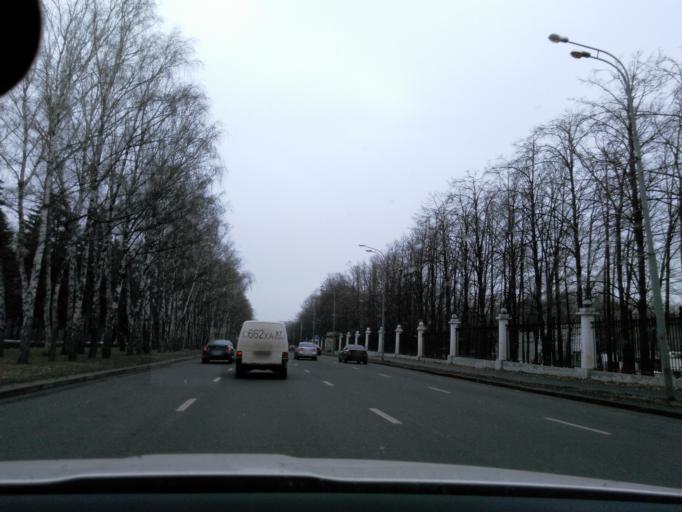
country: RU
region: Moscow
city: Vorob'yovo
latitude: 55.7036
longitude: 37.5404
